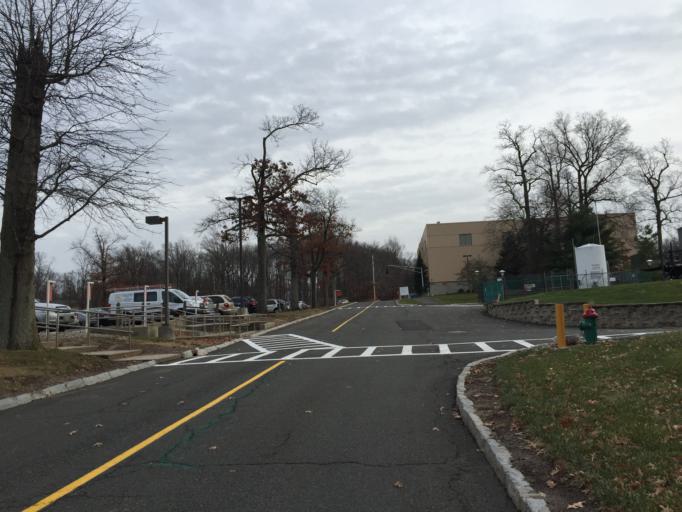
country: US
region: New Jersey
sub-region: Union County
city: New Providence
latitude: 40.6848
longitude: -74.3987
